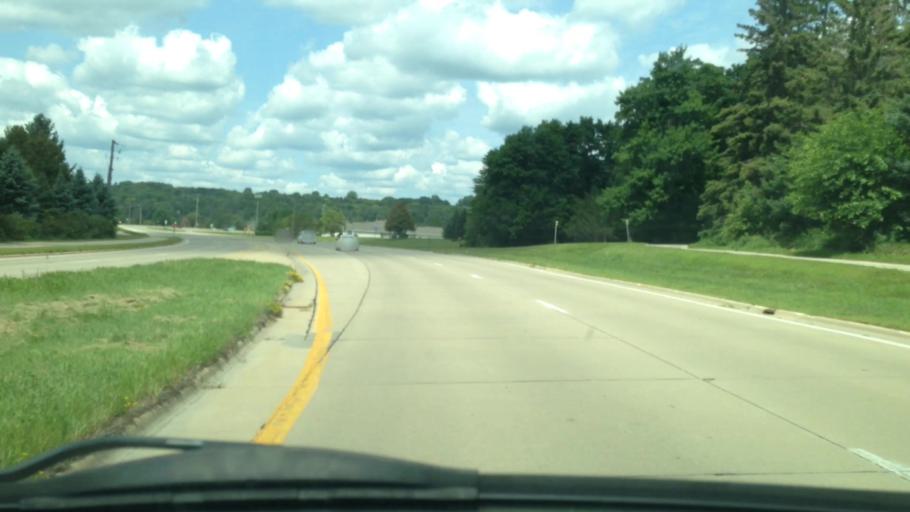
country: US
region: Minnesota
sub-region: Olmsted County
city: Rochester
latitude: 44.0018
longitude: -92.5025
